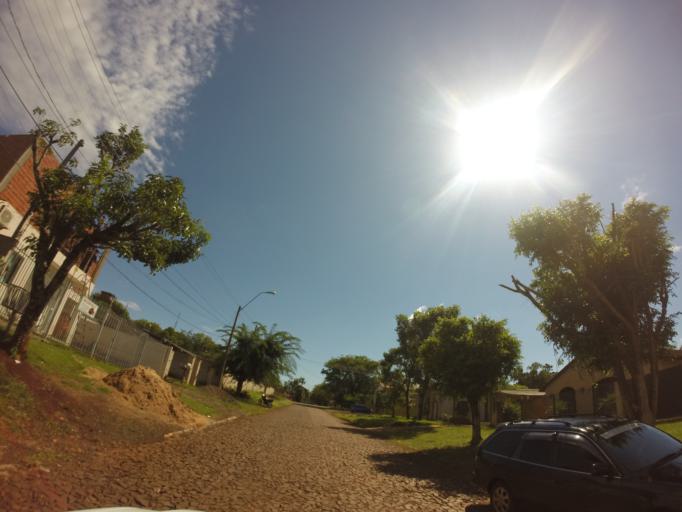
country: PY
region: Alto Parana
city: Ciudad del Este
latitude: -25.4116
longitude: -54.6396
